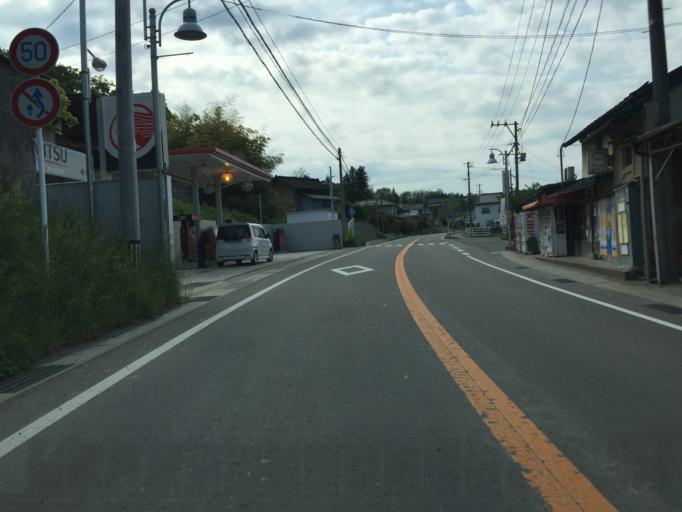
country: JP
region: Fukushima
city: Fukushima-shi
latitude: 37.6681
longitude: 140.5295
